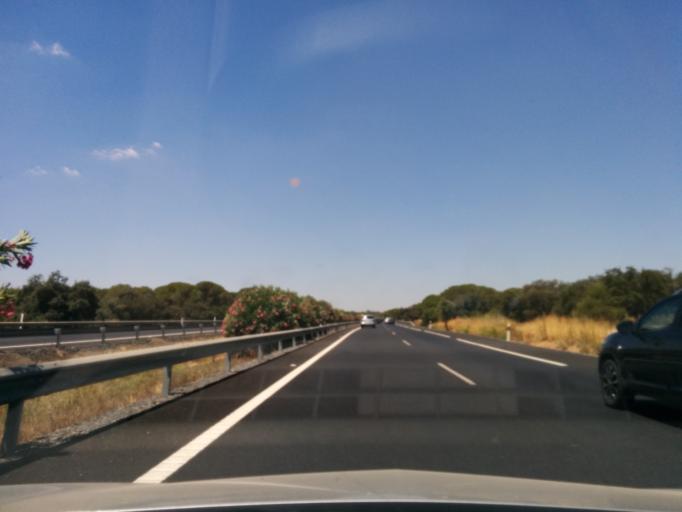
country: ES
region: Andalusia
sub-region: Provincia de Huelva
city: Manzanilla
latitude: 37.3467
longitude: -6.4586
